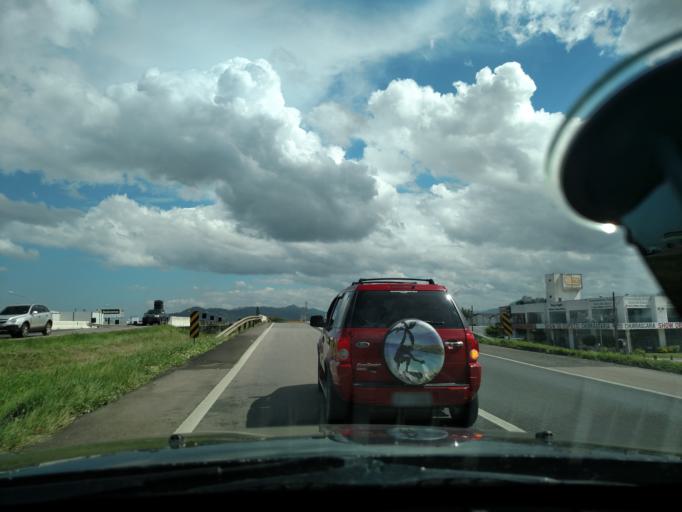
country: BR
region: Santa Catarina
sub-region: Tijucas
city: Tijucas
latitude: -27.2302
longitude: -48.6294
